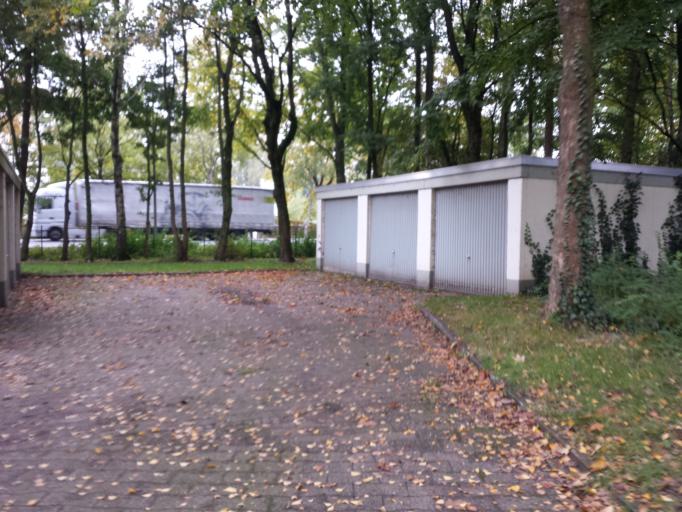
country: DE
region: North Rhine-Westphalia
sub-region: Regierungsbezirk Detmold
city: Guetersloh
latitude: 51.9183
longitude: 8.3580
